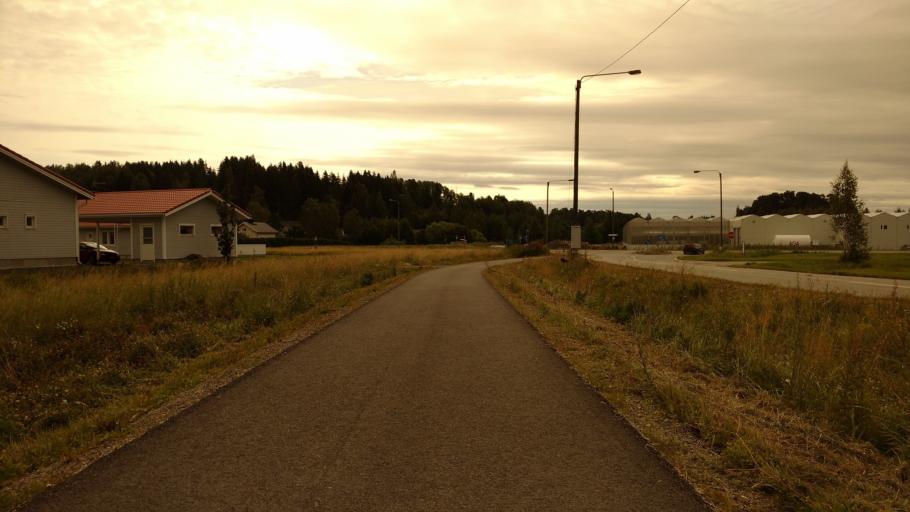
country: FI
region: Varsinais-Suomi
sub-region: Turku
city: Piikkioe
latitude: 60.4266
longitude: 22.4850
